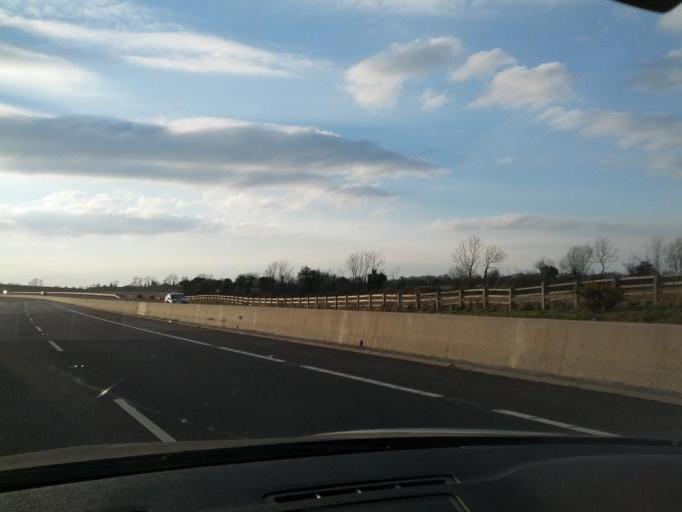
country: IE
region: Munster
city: Nenagh Bridge
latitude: 52.8684
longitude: -8.0697
